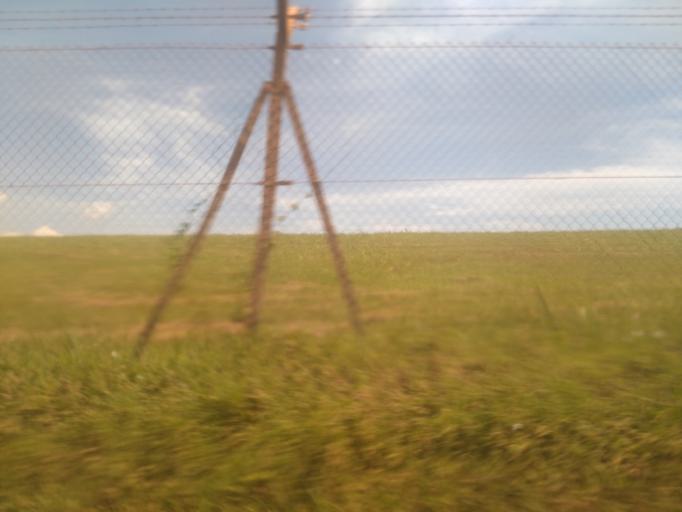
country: UG
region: Central Region
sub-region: Wakiso District
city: Entebbe
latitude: 0.0553
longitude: 32.4345
